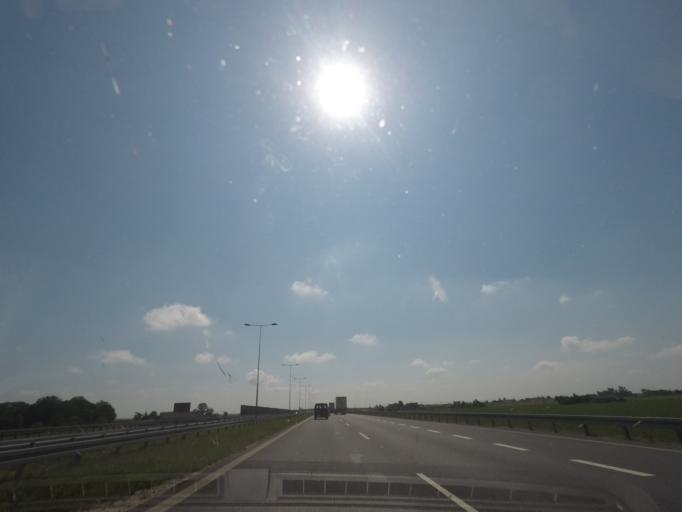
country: PL
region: Kujawsko-Pomorskie
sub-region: Powiat wloclawski
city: Chocen
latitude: 52.5649
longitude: 19.0176
